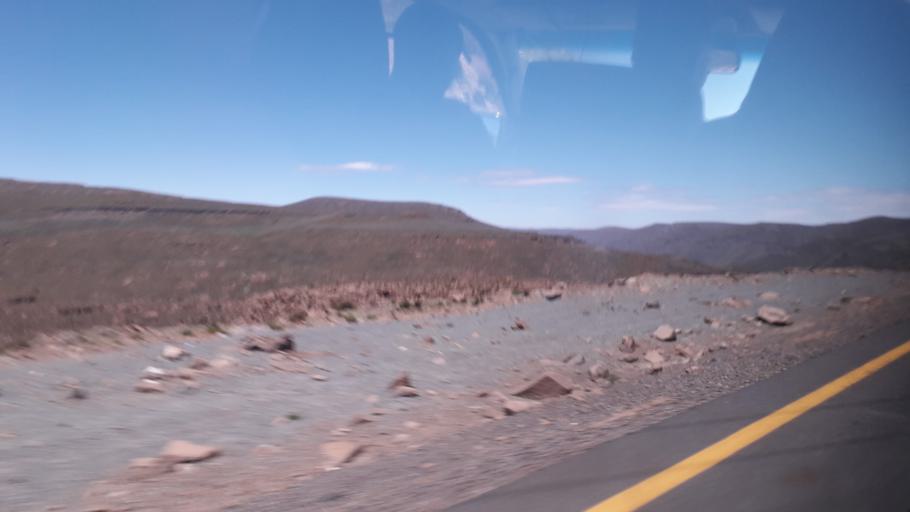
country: ZA
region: Orange Free State
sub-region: Thabo Mofutsanyana District Municipality
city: Phuthaditjhaba
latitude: -28.8341
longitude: 28.7422
